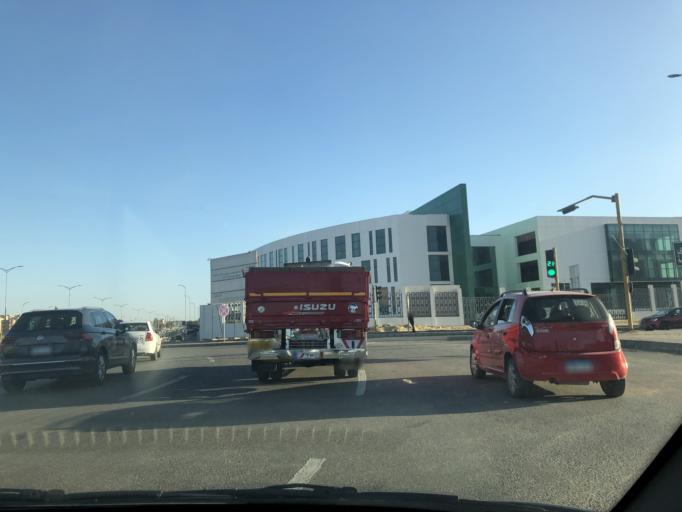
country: EG
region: Al Jizah
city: Madinat Sittah Uktubar
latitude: 29.9511
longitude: 30.9117
